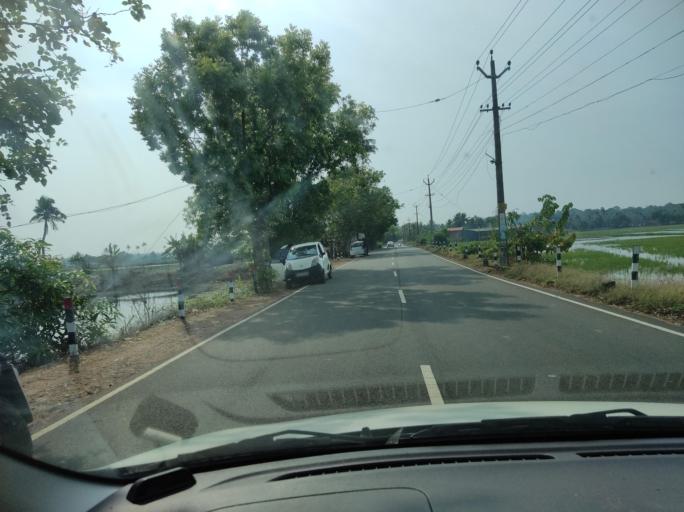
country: IN
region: Kerala
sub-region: Kottayam
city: Kottayam
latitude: 9.6913
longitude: 76.4949
